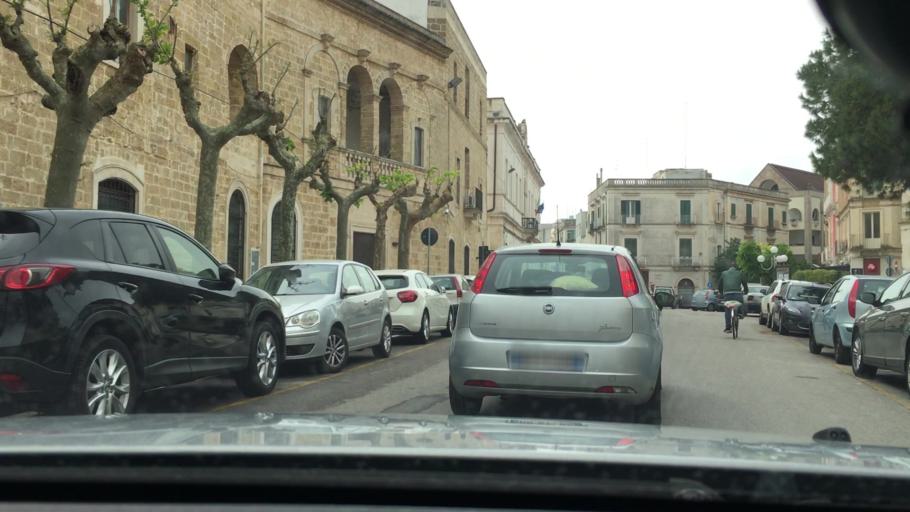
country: IT
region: Apulia
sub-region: Provincia di Bari
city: Gioia del Colle
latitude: 40.7986
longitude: 16.9214
